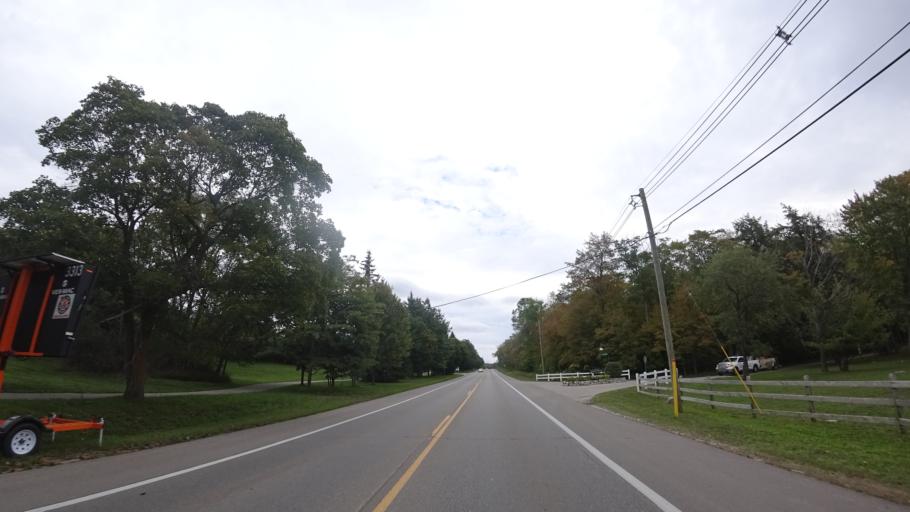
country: US
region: Michigan
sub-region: Emmet County
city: Harbor Springs
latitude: 45.4315
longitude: -84.9512
